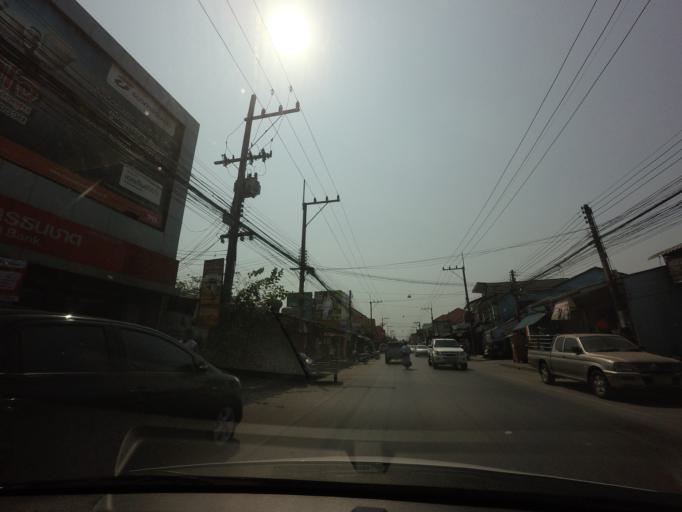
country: TH
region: Nakhon Pathom
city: Sam Phran
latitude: 13.7021
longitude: 100.2452
